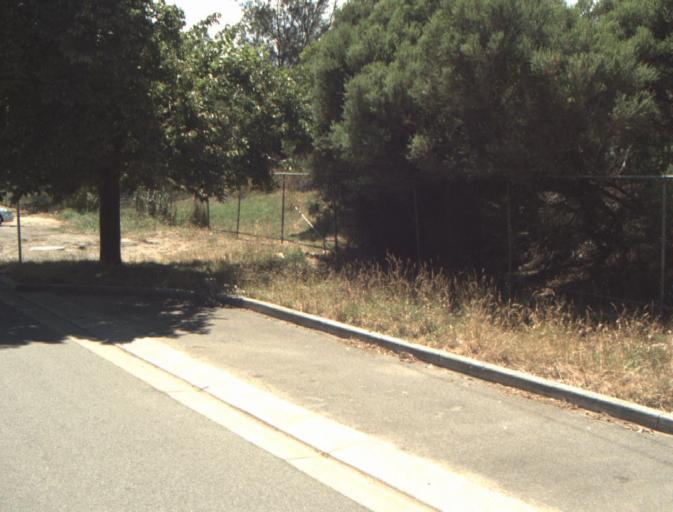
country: AU
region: Tasmania
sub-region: Launceston
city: West Launceston
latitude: -41.4564
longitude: 147.1422
